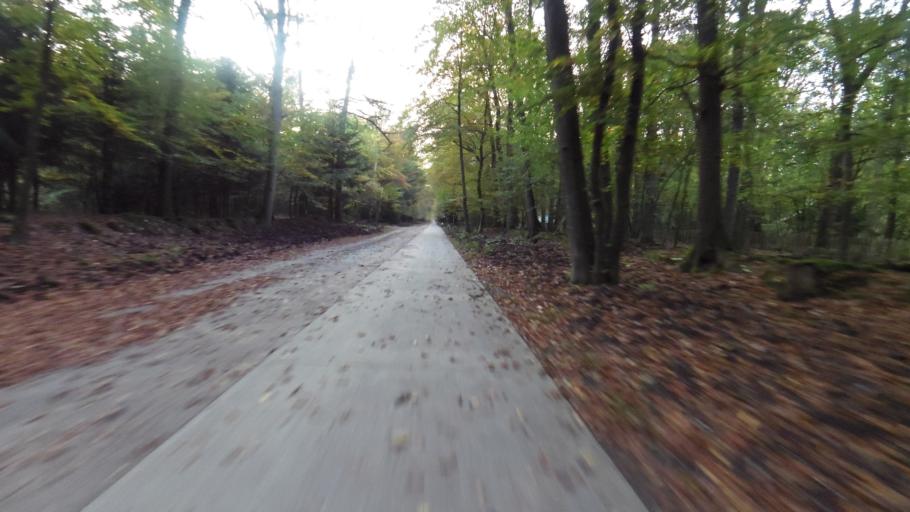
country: NL
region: Gelderland
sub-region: Gemeente Epe
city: Epe
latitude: 52.3561
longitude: 5.9053
